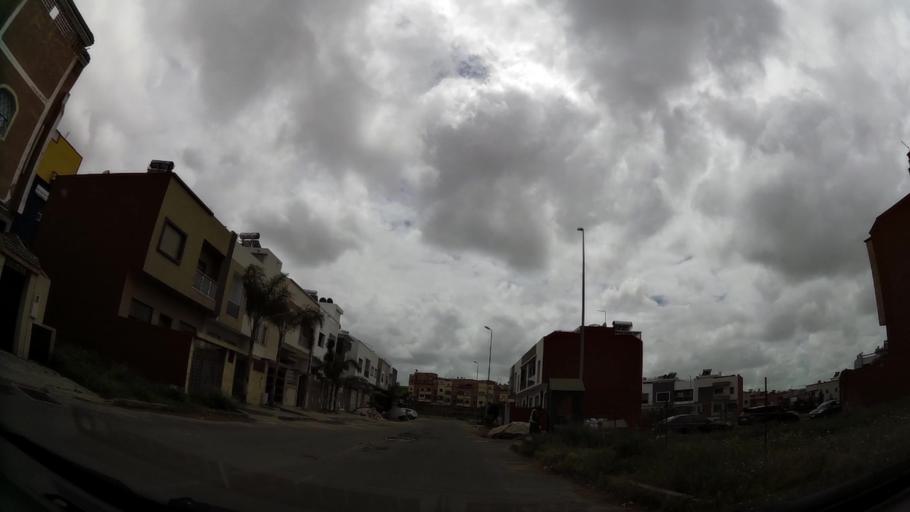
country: MA
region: Grand Casablanca
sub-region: Casablanca
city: Casablanca
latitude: 33.5311
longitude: -7.5969
